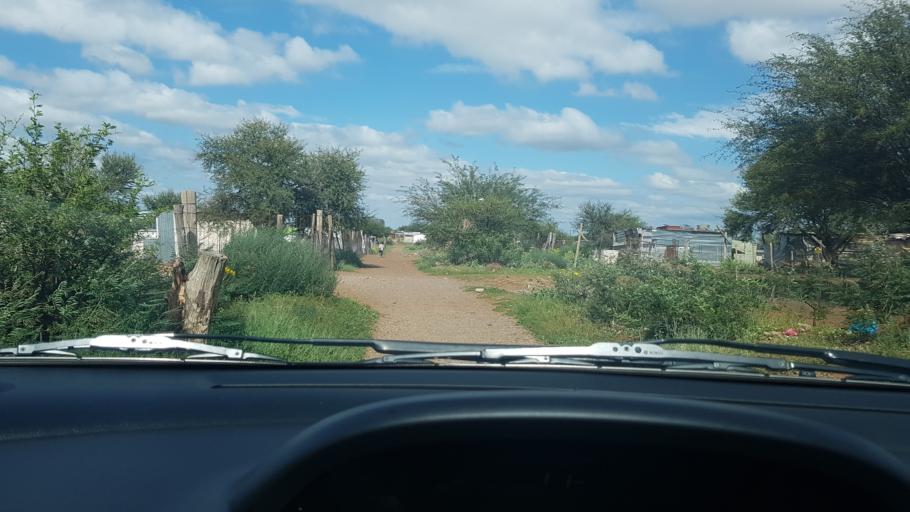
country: ZA
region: Northern Cape
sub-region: Siyanda District Municipality
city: Danielskuil
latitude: -28.1929
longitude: 23.5420
